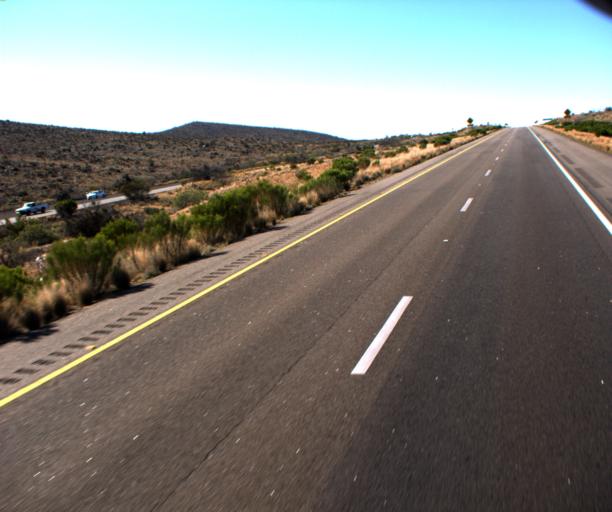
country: US
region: Arizona
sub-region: Mohave County
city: Kingman
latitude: 34.9603
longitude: -113.6703
